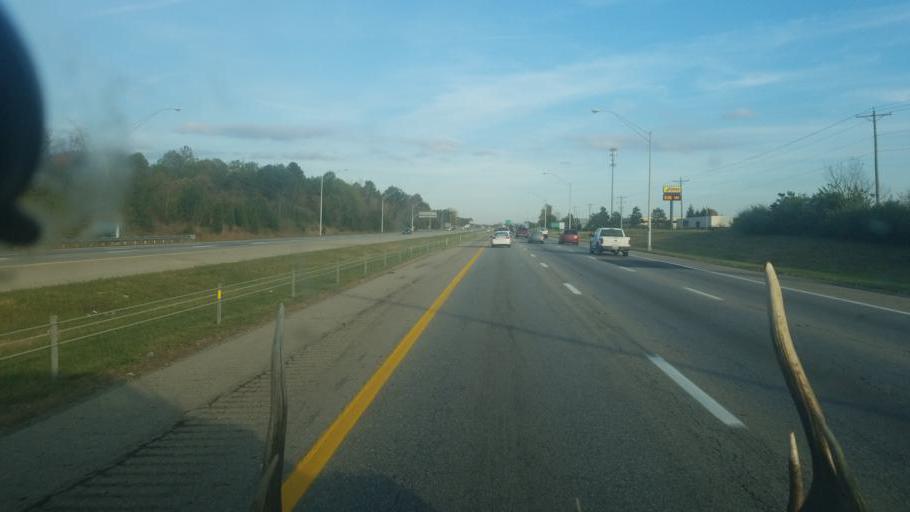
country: US
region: Ohio
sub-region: Franklin County
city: Reynoldsburg
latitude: 39.9317
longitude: -82.8186
